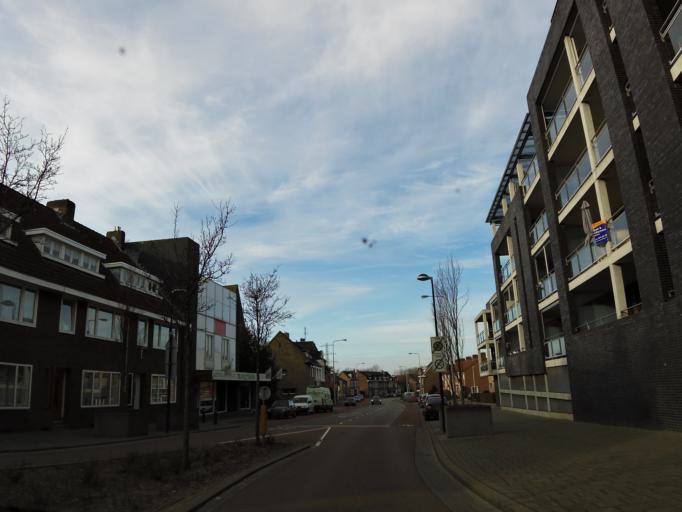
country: NL
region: Limburg
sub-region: Gemeente Heerlen
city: Nieuw-Lotbroek
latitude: 50.9155
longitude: 5.9537
